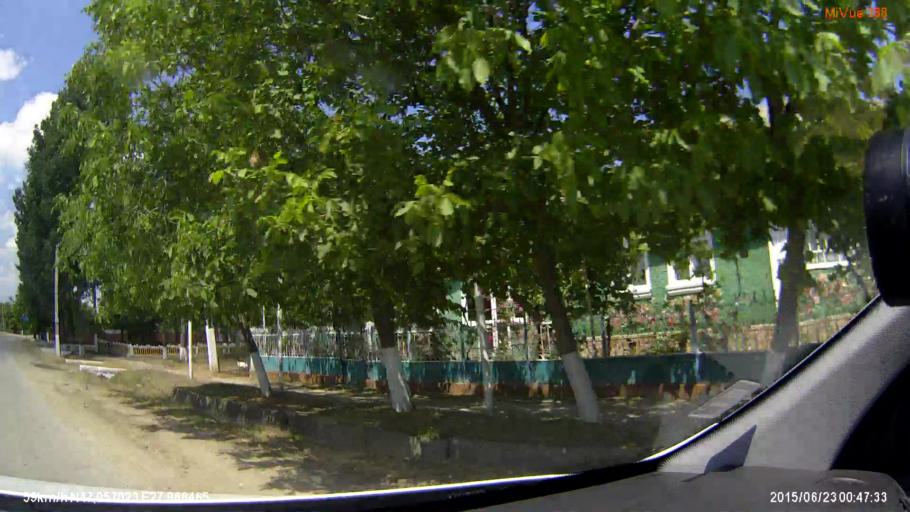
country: RO
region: Iasi
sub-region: Comuna Prisacani
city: Prisacani
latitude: 47.0569
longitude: 27.9666
